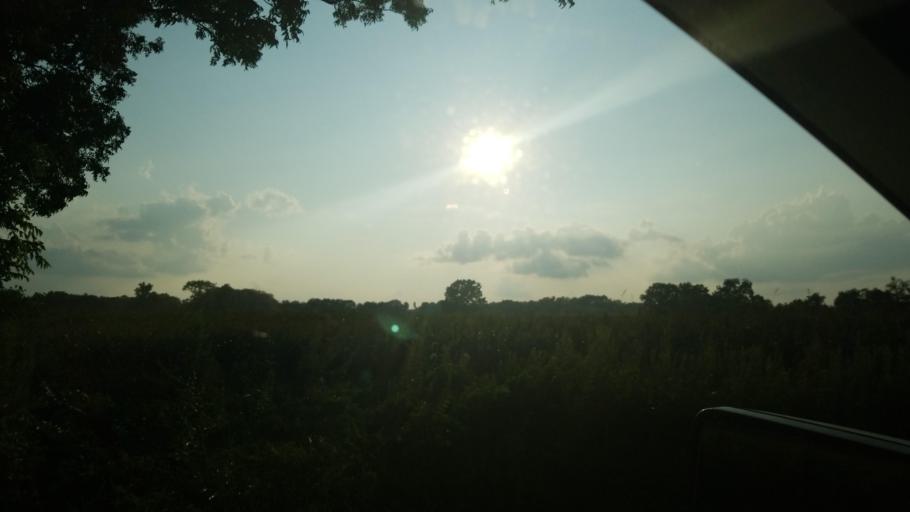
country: US
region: Illinois
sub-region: Saline County
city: Harrisburg
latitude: 37.8027
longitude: -88.6054
